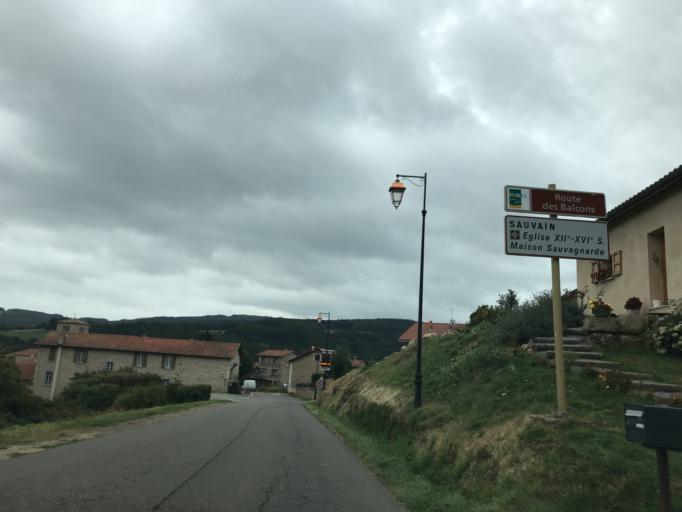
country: FR
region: Rhone-Alpes
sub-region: Departement de la Loire
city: Sail-sous-Couzan
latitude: 45.6752
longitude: 3.9039
